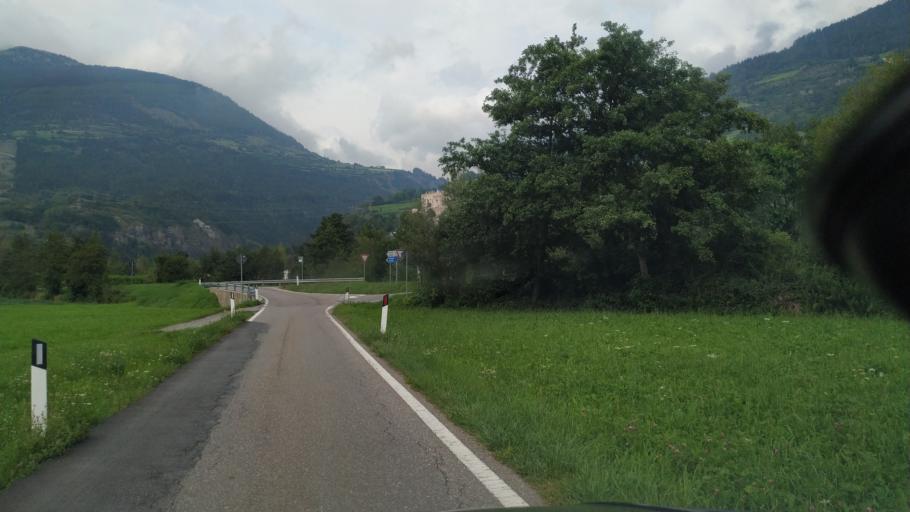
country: IT
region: Trentino-Alto Adige
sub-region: Bolzano
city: Sluderno
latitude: 46.6588
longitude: 10.5825
